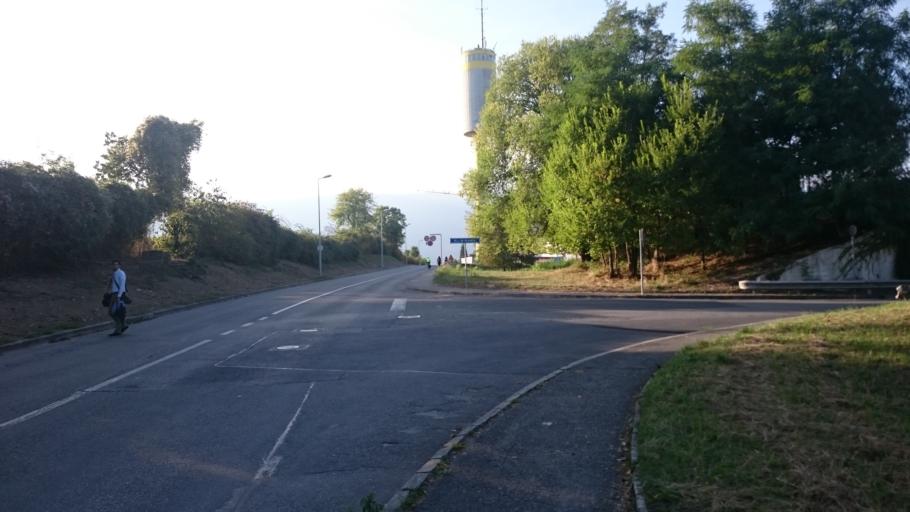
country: CH
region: Geneva
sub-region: Geneva
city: Satigny
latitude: 46.2335
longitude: 6.0437
